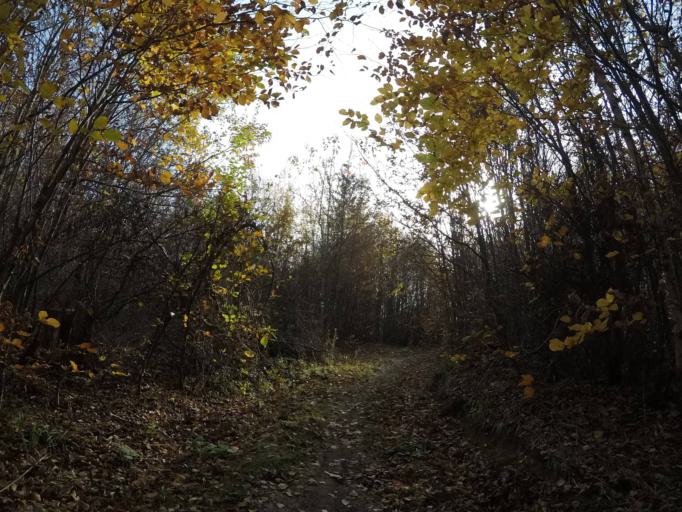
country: SK
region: Presovsky
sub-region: Okres Presov
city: Presov
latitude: 48.9640
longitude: 21.1829
